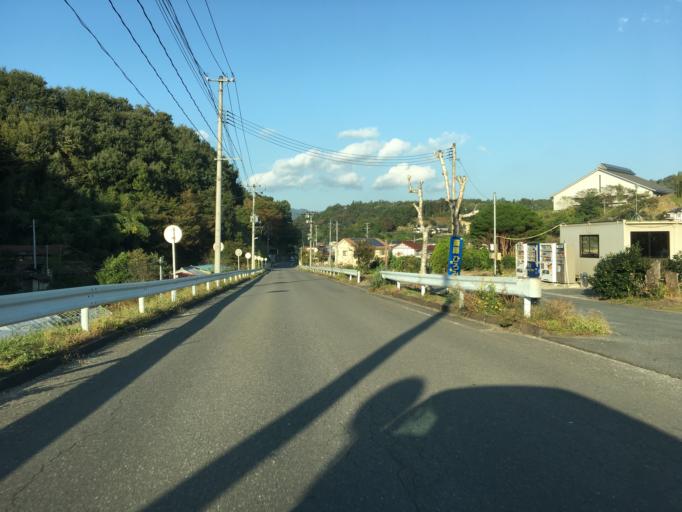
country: JP
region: Fukushima
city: Fukushima-shi
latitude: 37.6557
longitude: 140.5908
